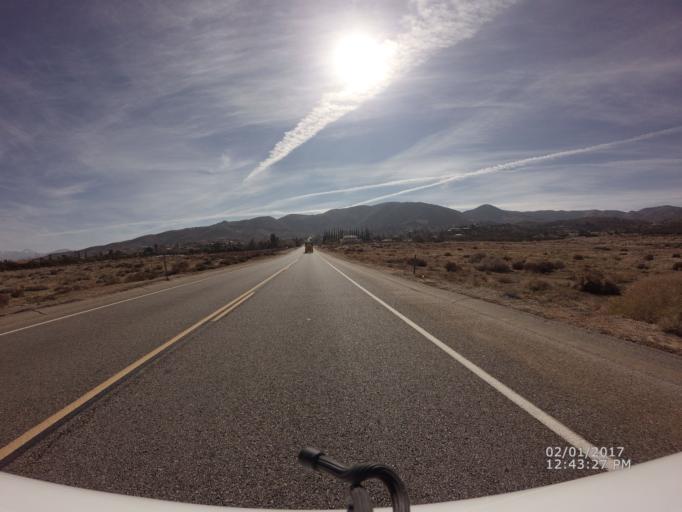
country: US
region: California
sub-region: Los Angeles County
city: Palmdale
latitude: 34.5516
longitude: -118.1414
